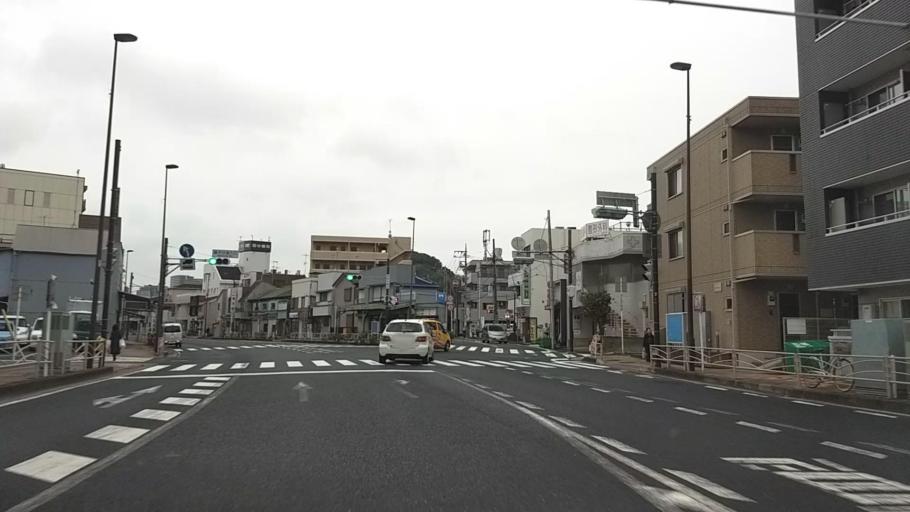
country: JP
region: Kanagawa
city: Yokohama
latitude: 35.4117
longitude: 139.6227
